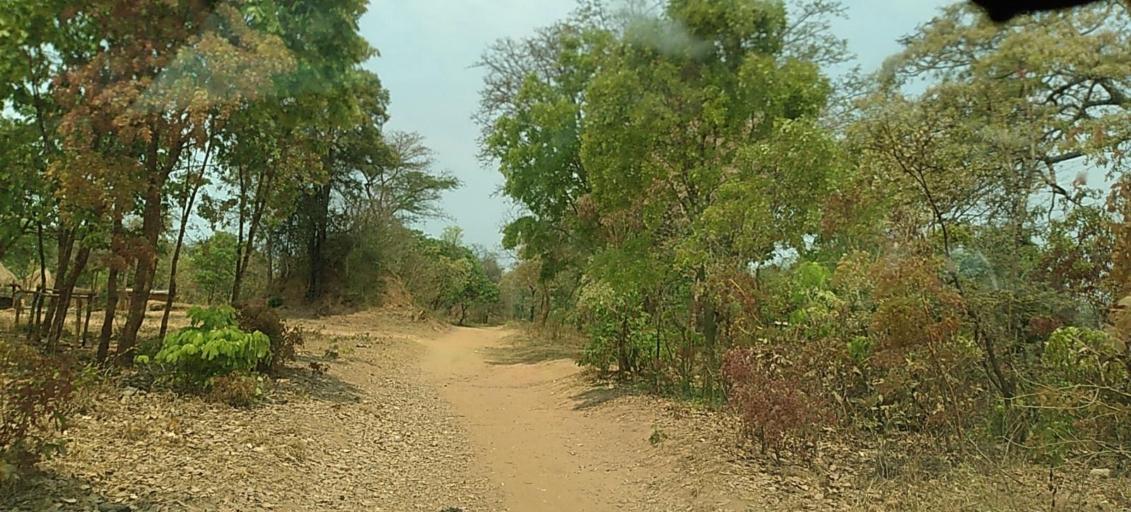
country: ZM
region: North-Western
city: Kabompo
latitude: -13.5722
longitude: 24.4401
